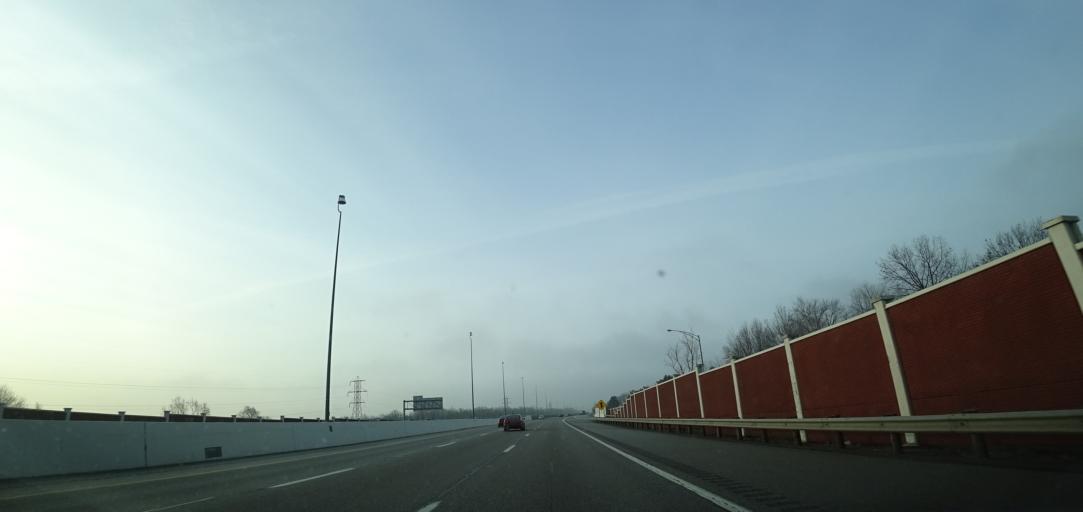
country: US
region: Ohio
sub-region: Cuyahoga County
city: Independence
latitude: 41.3600
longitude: -81.6501
